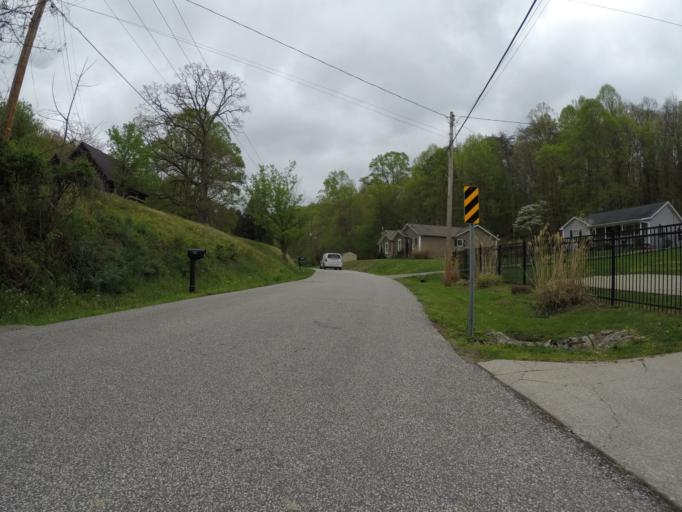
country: US
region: West Virginia
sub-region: Cabell County
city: Barboursville
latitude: 38.4051
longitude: -82.2823
